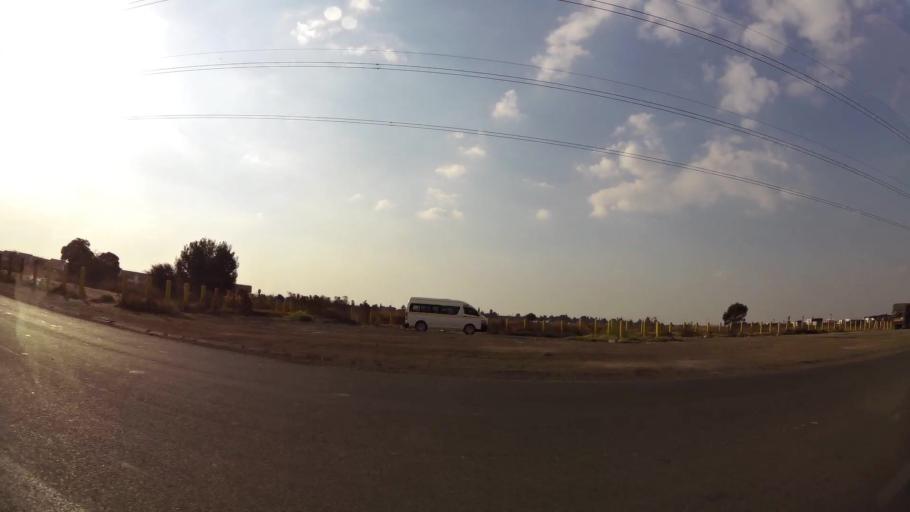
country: ZA
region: Gauteng
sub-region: City of Johannesburg Metropolitan Municipality
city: Modderfontein
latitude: -26.1083
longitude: 28.1944
